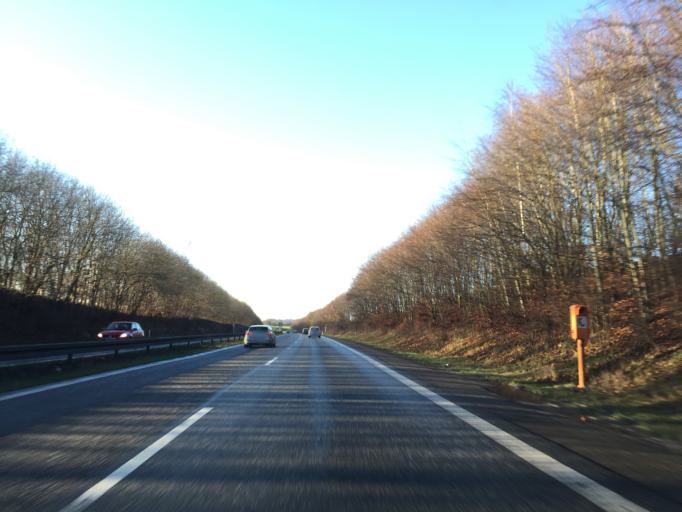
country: DK
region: South Denmark
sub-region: Odense Kommune
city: Bellinge
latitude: 55.3822
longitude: 10.2643
